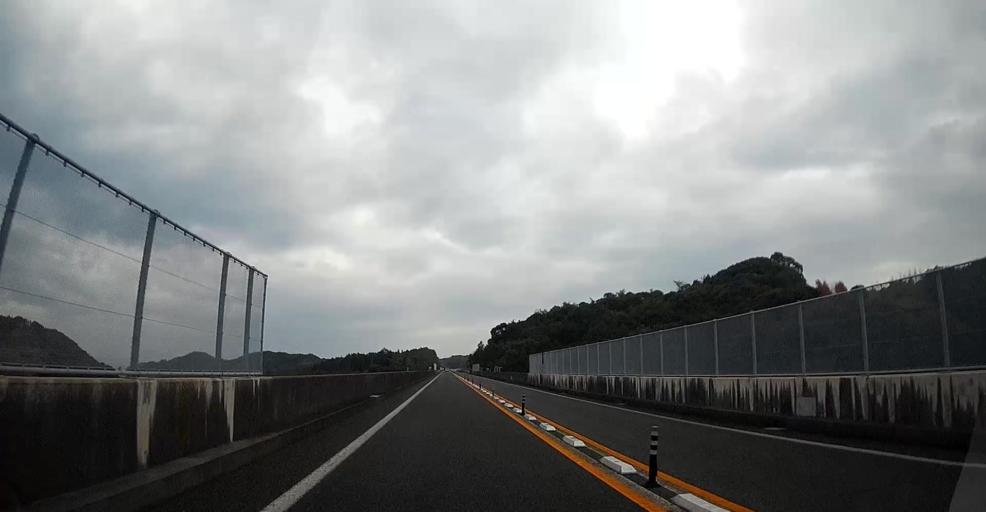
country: JP
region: Kumamoto
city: Hondo
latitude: 32.5097
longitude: 130.3509
